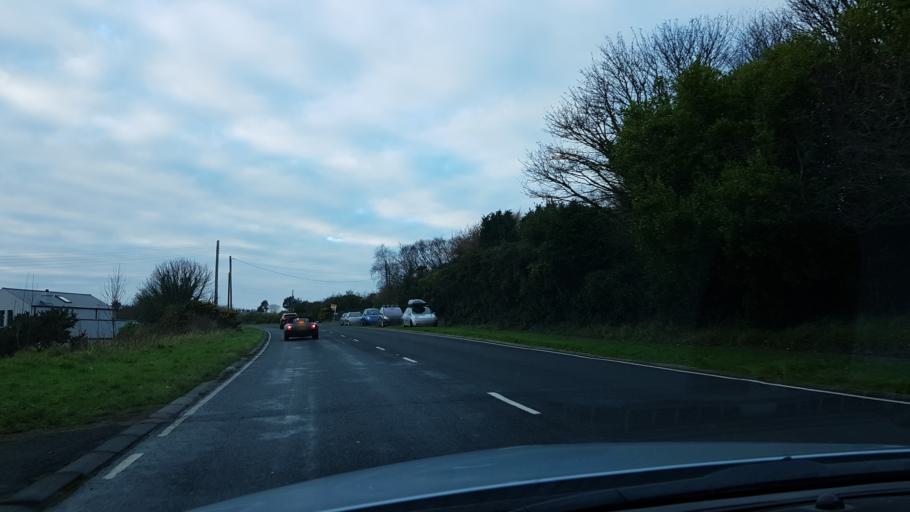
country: GB
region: Northern Ireland
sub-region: Down District
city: Donaghadee
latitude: 54.6704
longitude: -5.5783
